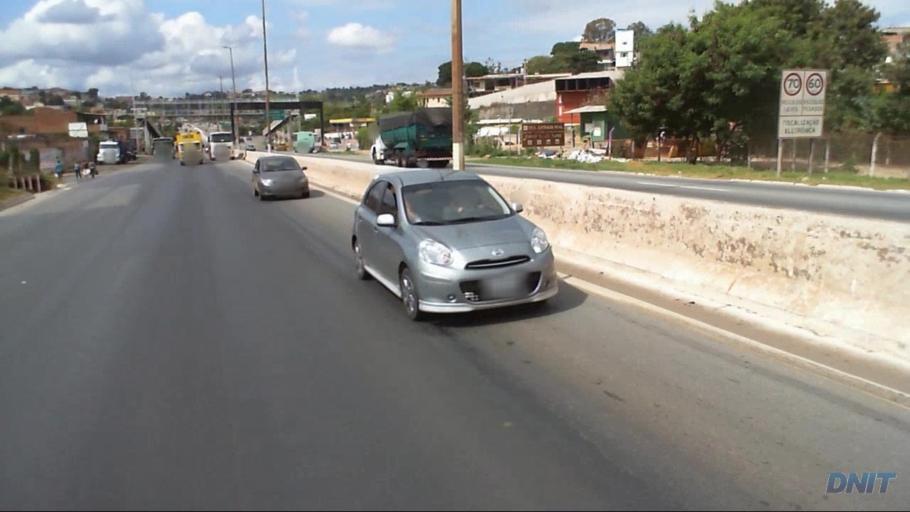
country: BR
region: Minas Gerais
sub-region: Belo Horizonte
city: Belo Horizonte
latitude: -19.8573
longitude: -43.9027
